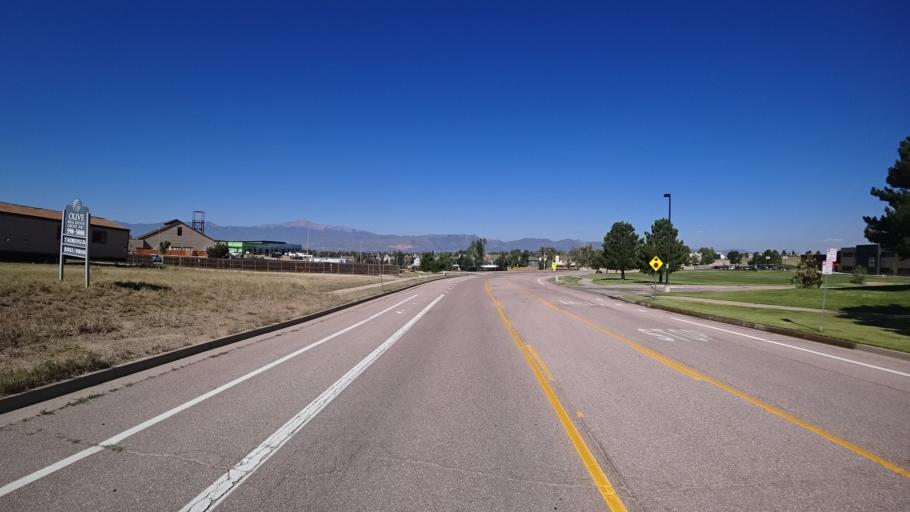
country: US
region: Colorado
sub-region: El Paso County
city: Black Forest
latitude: 38.9577
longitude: -104.7359
